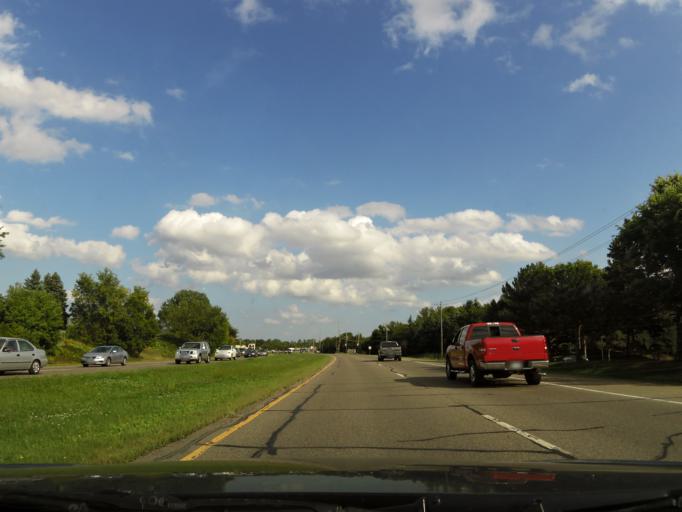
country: US
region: Minnesota
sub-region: Dakota County
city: Burnsville
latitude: 44.7388
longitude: -93.2665
